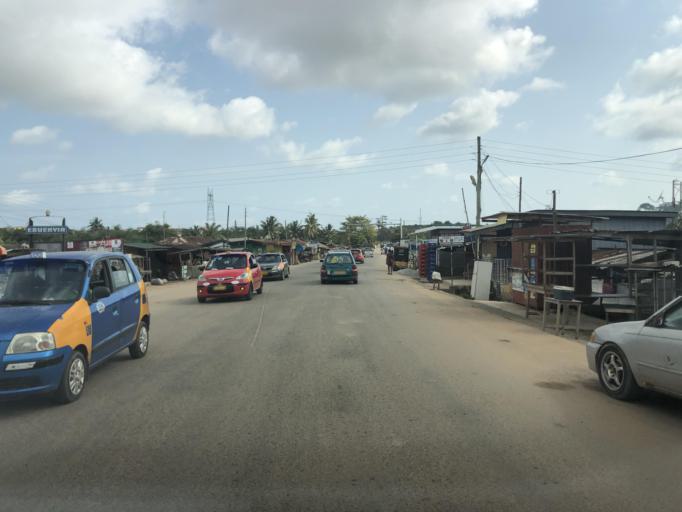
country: GH
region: Central
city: Cape Coast
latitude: 5.1502
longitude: -1.2885
